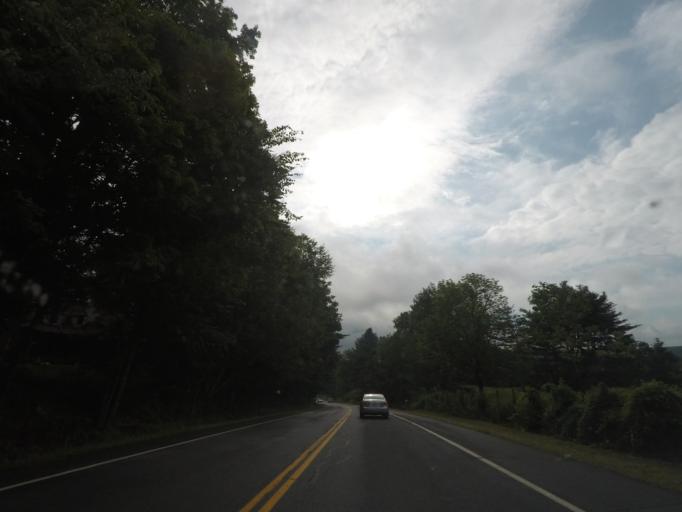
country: US
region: New York
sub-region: Rensselaer County
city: Nassau
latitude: 42.4953
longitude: -73.5385
